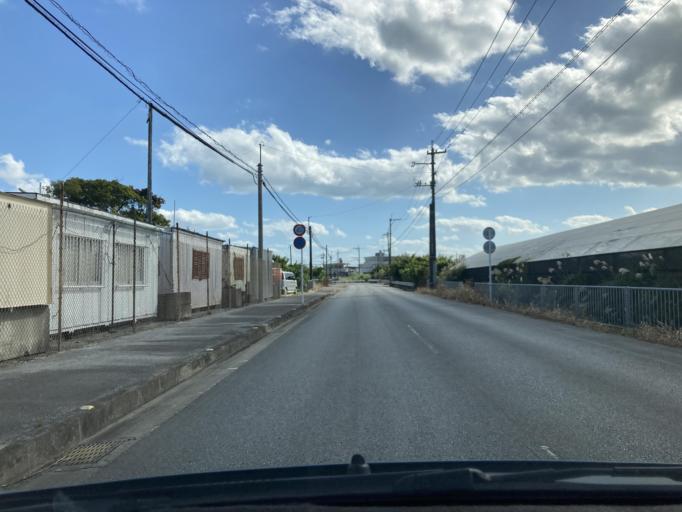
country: JP
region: Okinawa
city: Gushikawa
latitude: 26.3459
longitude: 127.8475
